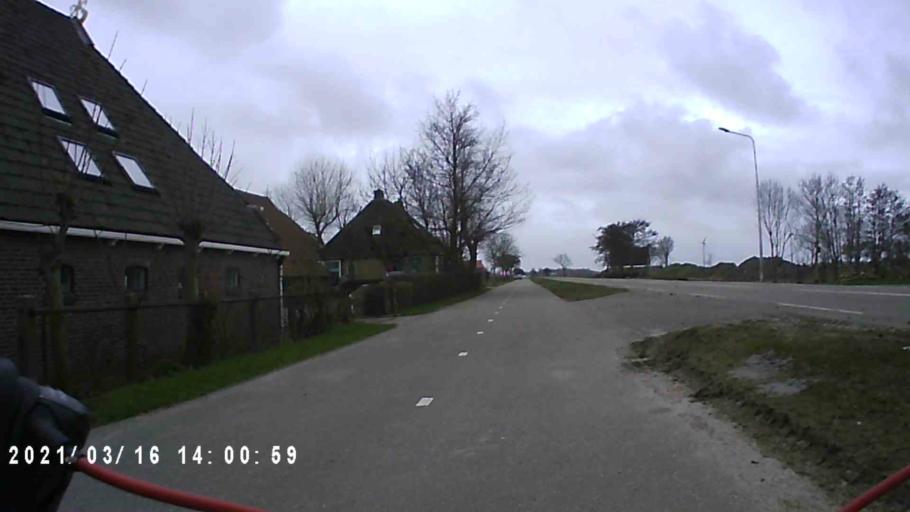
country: NL
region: Friesland
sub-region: Gemeente Franekeradeel
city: Sexbierum
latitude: 53.1844
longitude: 5.4901
